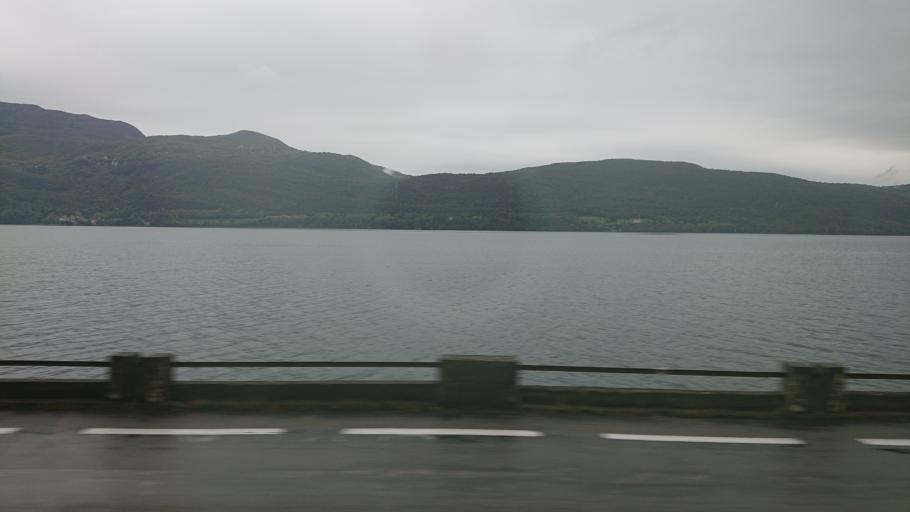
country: FR
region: Rhone-Alpes
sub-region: Departement de la Savoie
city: Chatillon
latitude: 45.7760
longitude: 5.8659
